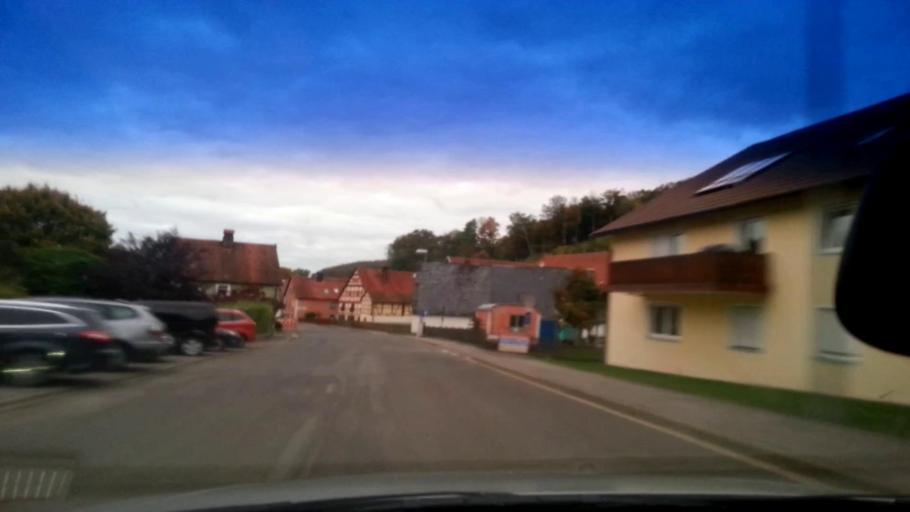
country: DE
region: Bavaria
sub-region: Upper Franconia
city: Poxdorf
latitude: 49.9790
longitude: 11.0932
